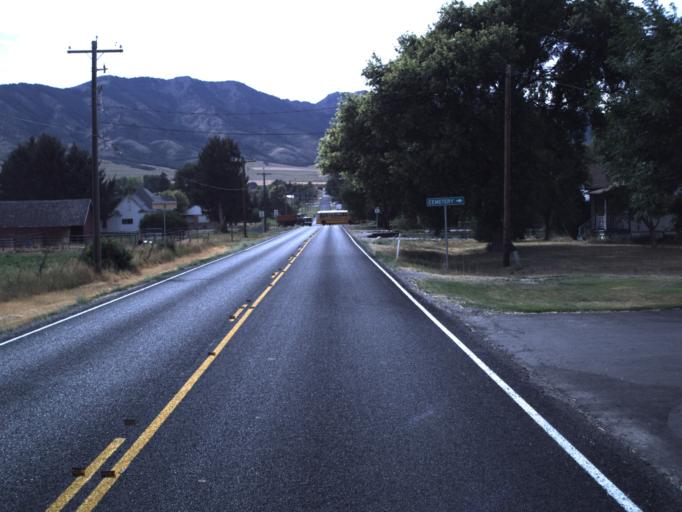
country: US
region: Utah
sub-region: Cache County
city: Benson
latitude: 41.9200
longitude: -112.0427
